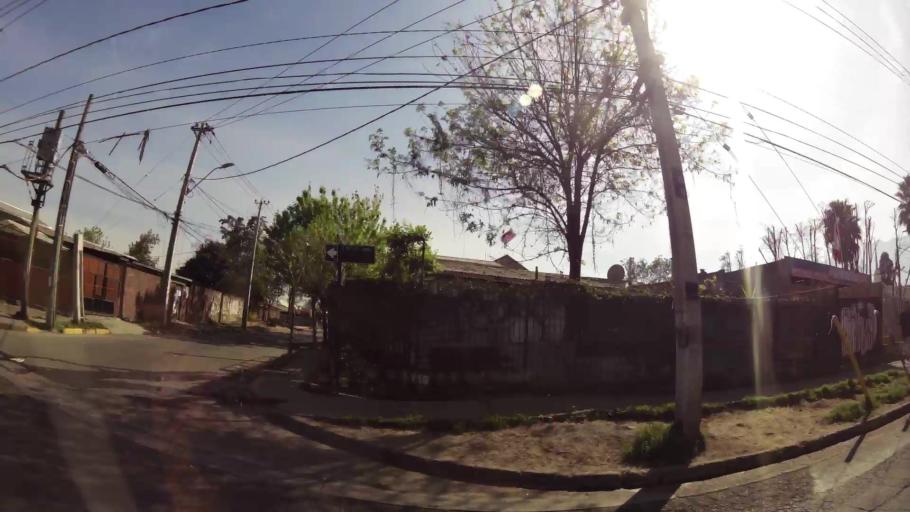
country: CL
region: Santiago Metropolitan
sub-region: Provincia de Santiago
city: Villa Presidente Frei, Nunoa, Santiago, Chile
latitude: -33.5034
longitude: -70.5707
